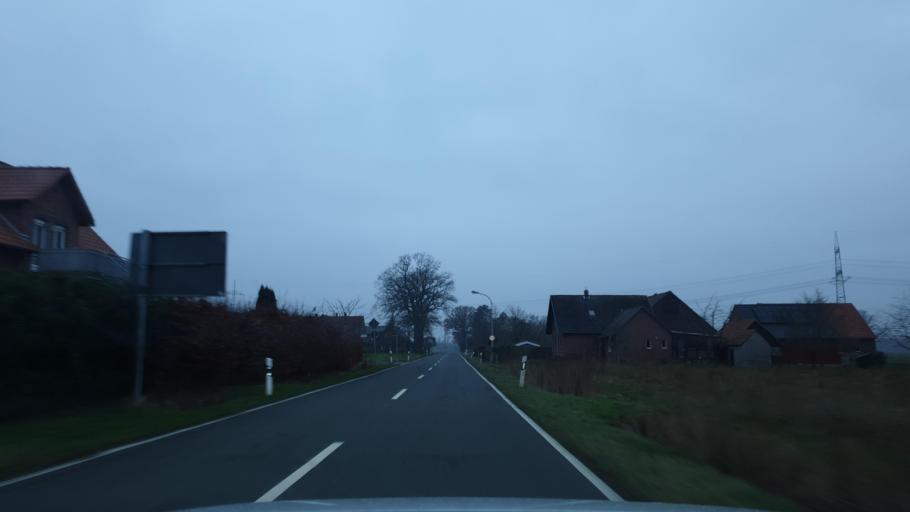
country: DE
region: North Rhine-Westphalia
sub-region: Regierungsbezirk Detmold
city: Petershagen
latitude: 52.3656
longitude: 8.9006
